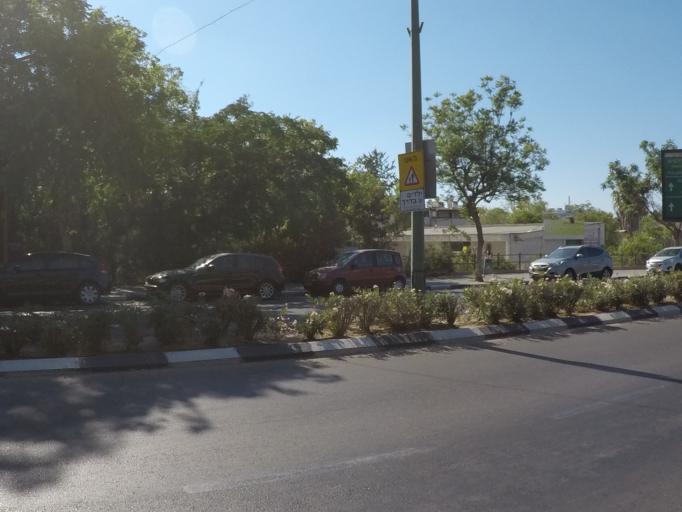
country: IL
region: Tel Aviv
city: Ramat Gan
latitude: 32.1081
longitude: 34.8014
